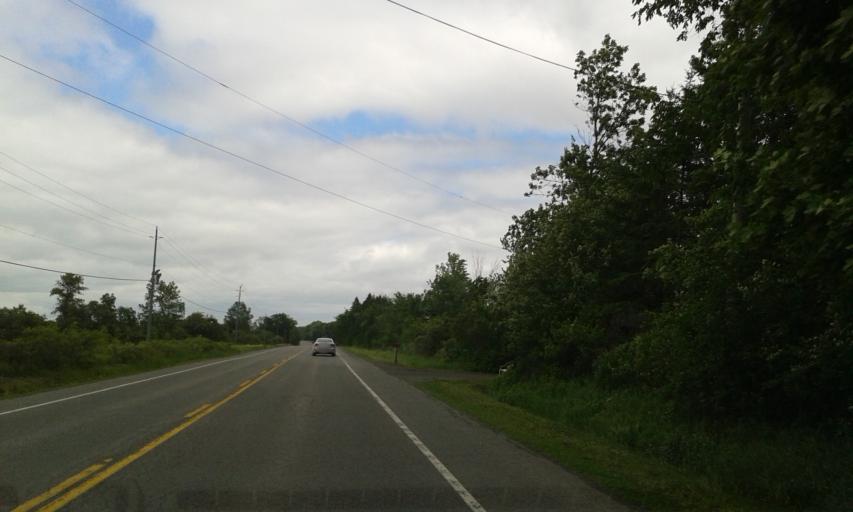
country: CA
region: Ontario
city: Picton
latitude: 44.0574
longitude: -77.0246
